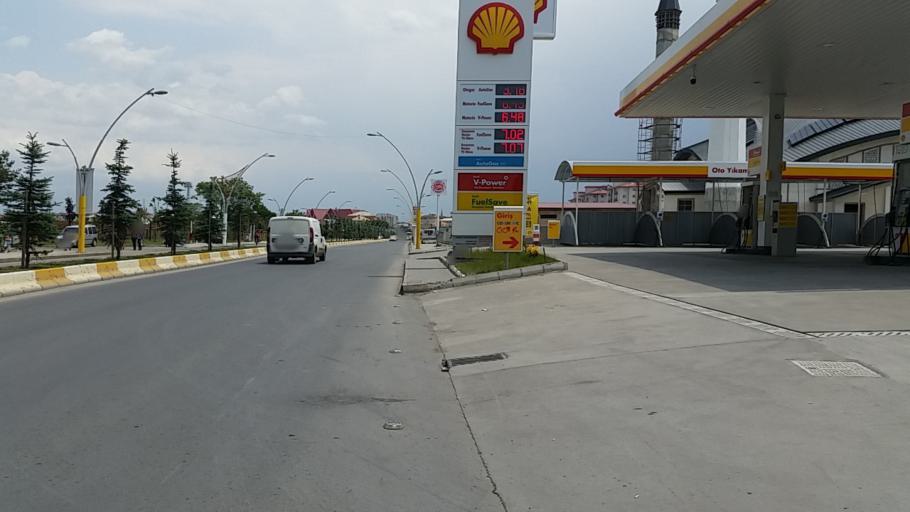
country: TR
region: Agri
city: Agri
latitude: 39.7189
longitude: 43.0334
